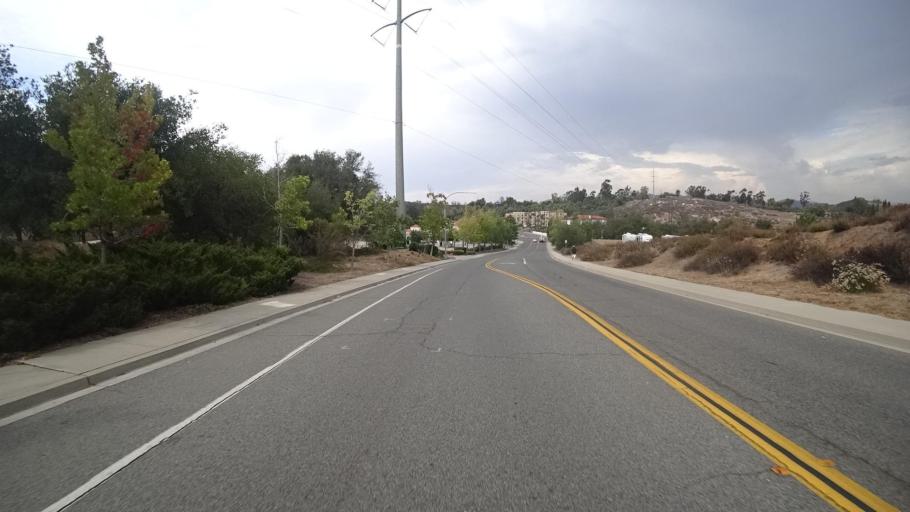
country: US
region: California
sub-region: San Diego County
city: Escondido
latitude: 33.1444
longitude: -117.1036
